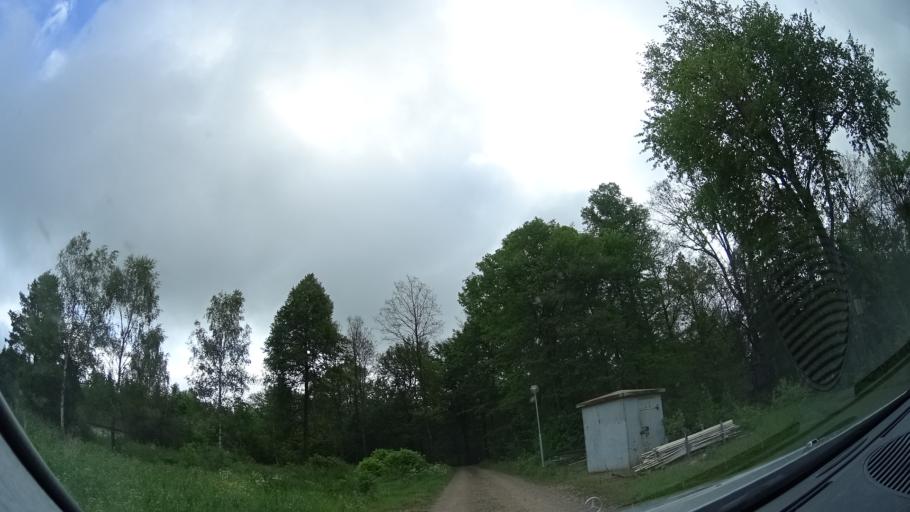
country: SE
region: Skane
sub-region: Hoors Kommun
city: Hoeoer
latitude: 55.9694
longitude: 13.4568
